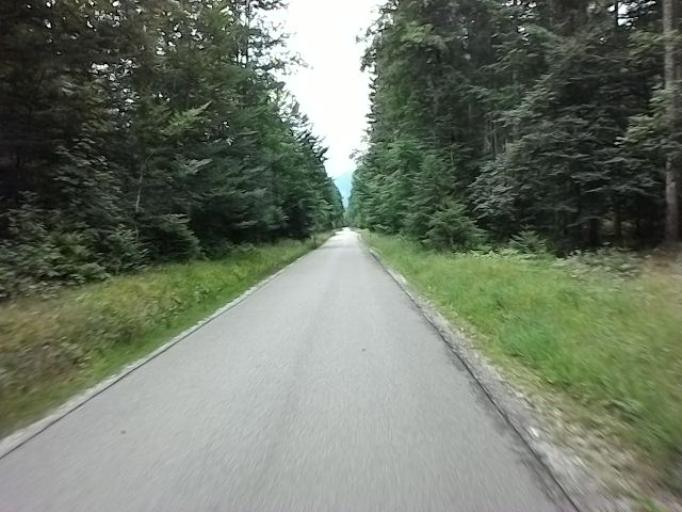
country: DE
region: Bavaria
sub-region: Upper Bavaria
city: Jachenau
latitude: 47.5479
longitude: 11.3742
